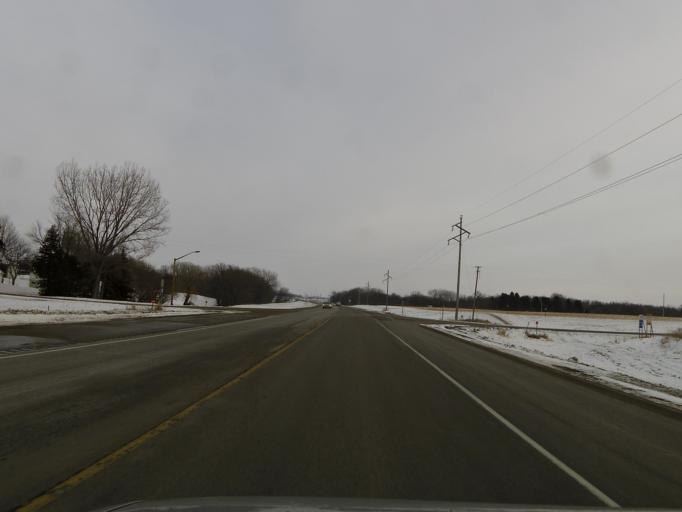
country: US
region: Minnesota
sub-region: Carver County
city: Mayer
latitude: 44.9056
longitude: -93.8909
